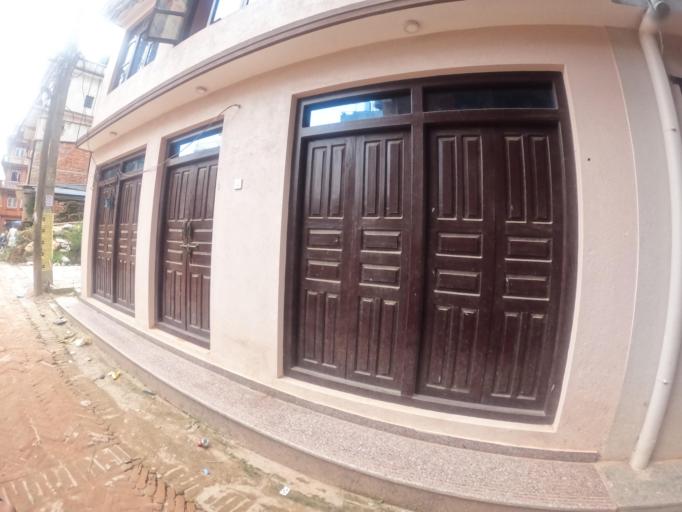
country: NP
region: Central Region
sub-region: Bagmati Zone
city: Bhaktapur
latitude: 27.6853
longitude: 85.3855
